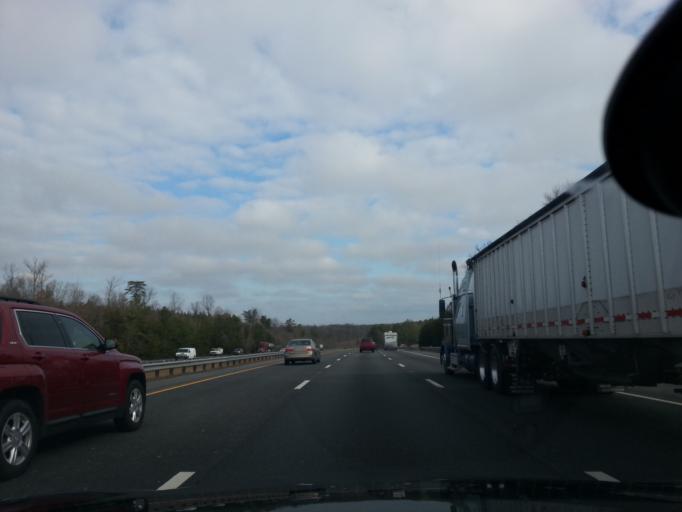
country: US
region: Virginia
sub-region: Spotsylvania County
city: Spotsylvania Courthouse
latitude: 38.1572
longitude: -77.5071
